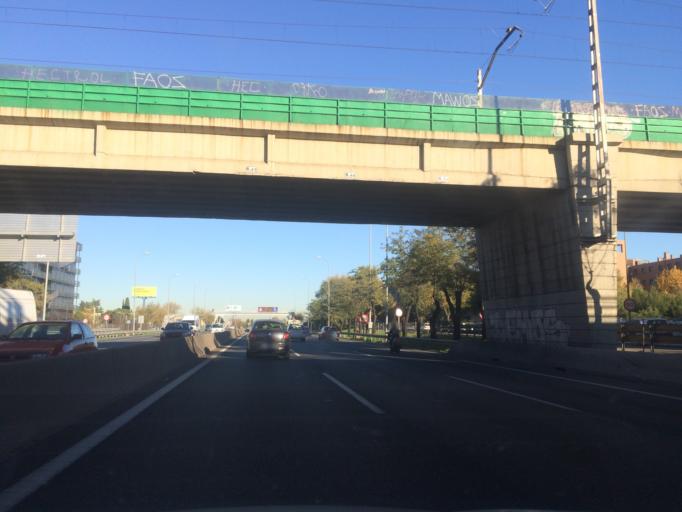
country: ES
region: Madrid
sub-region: Provincia de Madrid
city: San Blas
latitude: 40.4498
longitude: -3.6040
